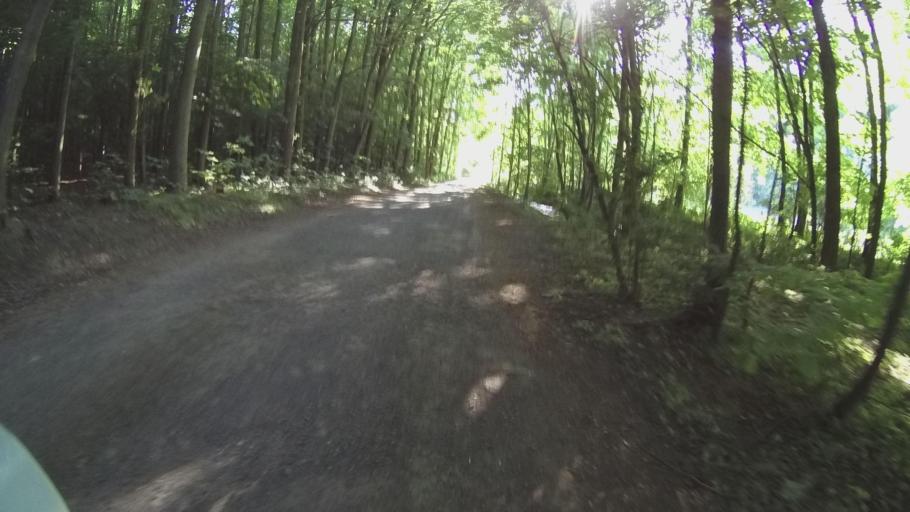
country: CZ
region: Central Bohemia
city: Zdiby
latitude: 50.1506
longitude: 14.4280
